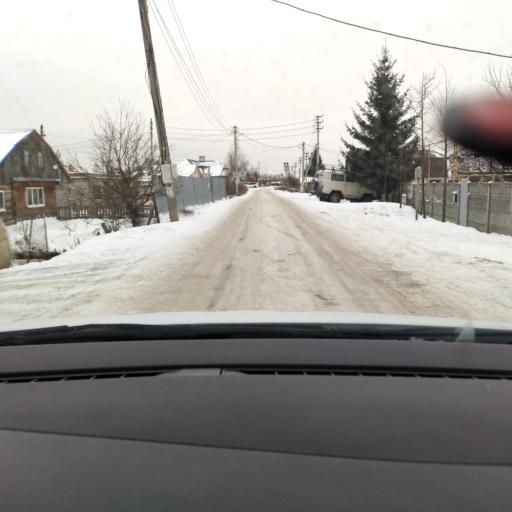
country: RU
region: Tatarstan
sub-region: Gorod Kazan'
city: Kazan
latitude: 55.9000
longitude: 49.1378
